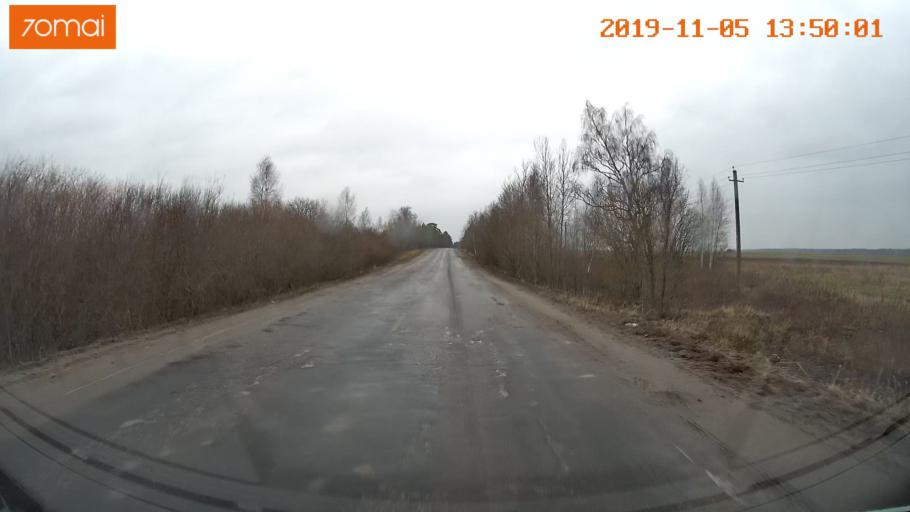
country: RU
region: Ivanovo
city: Kaminskiy
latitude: 57.0160
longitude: 41.4102
